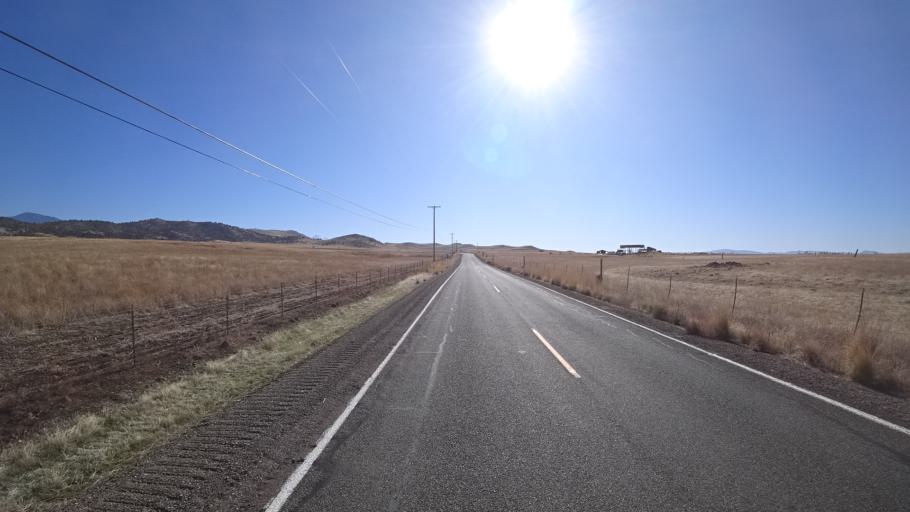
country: US
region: California
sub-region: Siskiyou County
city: Montague
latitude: 41.8070
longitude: -122.4158
